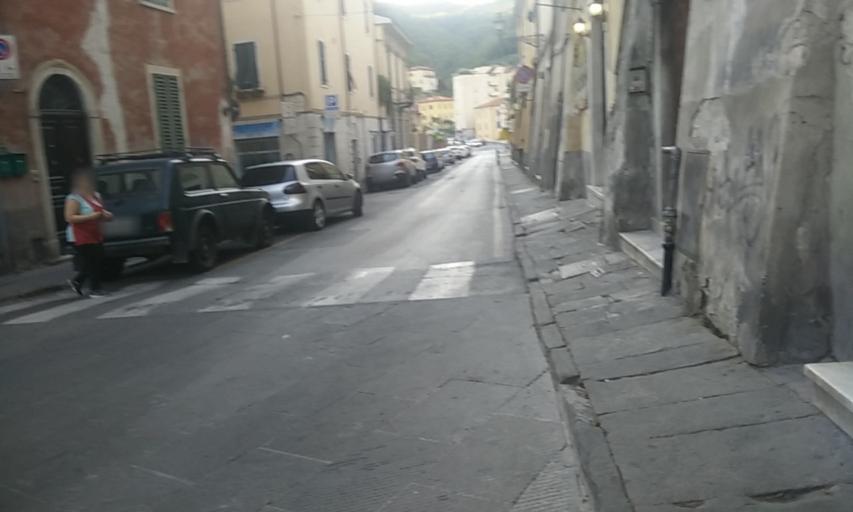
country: IT
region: Tuscany
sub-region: Provincia di Massa-Carrara
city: Carrara
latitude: 44.0790
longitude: 10.0974
